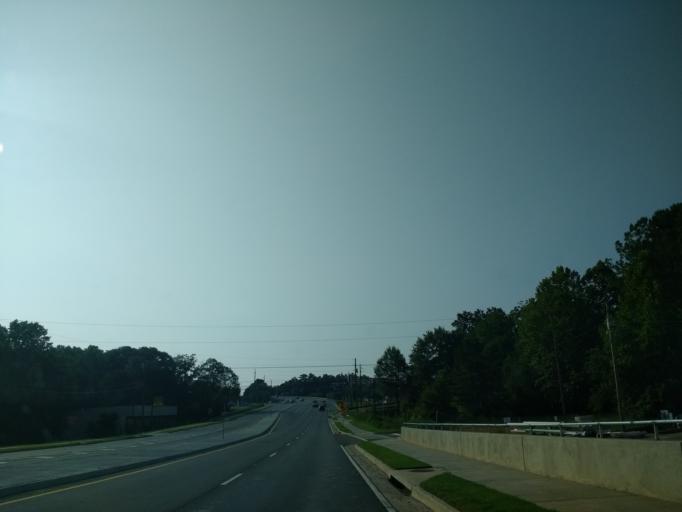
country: US
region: Georgia
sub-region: Gwinnett County
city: Sugar Hill
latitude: 34.1076
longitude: -84.0331
